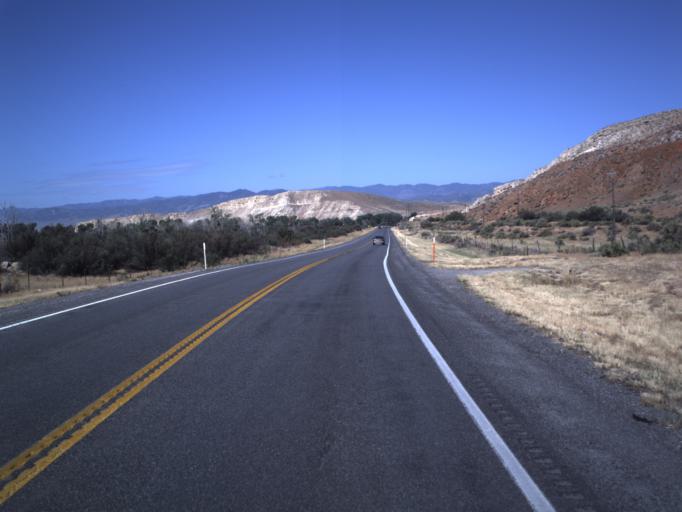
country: US
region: Utah
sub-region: Sanpete County
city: Gunnison
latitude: 39.1625
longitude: -111.7395
